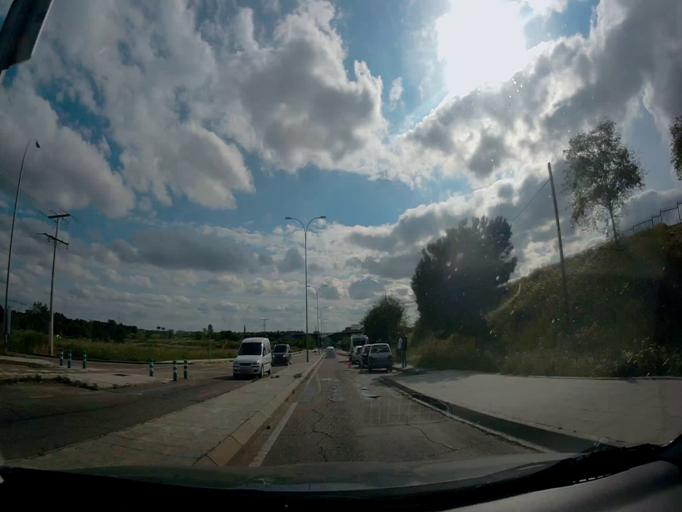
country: ES
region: Madrid
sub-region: Provincia de Madrid
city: Alcorcon
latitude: 40.3392
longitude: -3.8451
